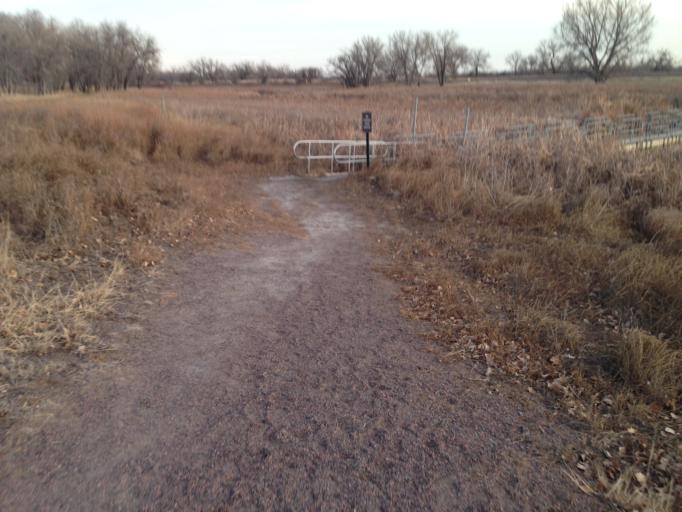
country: US
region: Colorado
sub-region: Adams County
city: Derby
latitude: 39.8147
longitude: -104.8529
